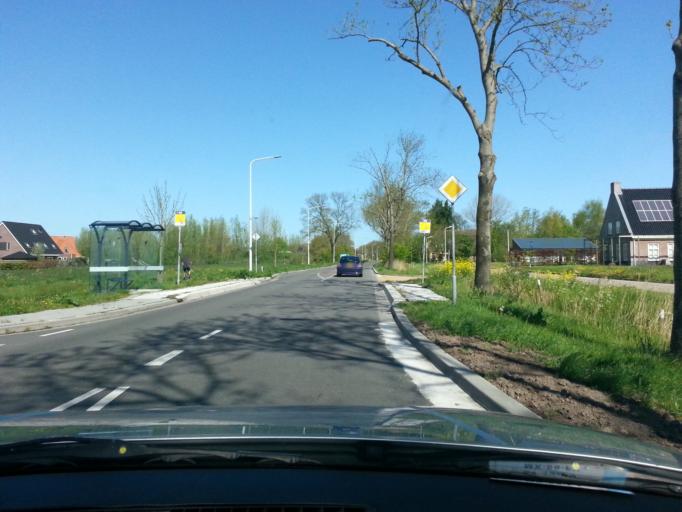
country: NL
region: Friesland
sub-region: Gemeente Achtkarspelen
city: Buitenpost
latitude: 53.2438
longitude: 6.1550
